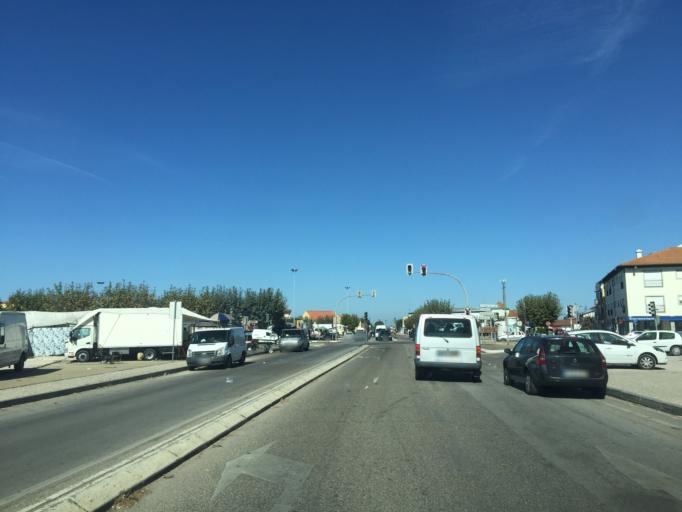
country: PT
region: Coimbra
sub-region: Montemor-O-Velho
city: Arazede
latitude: 40.3140
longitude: -8.7535
